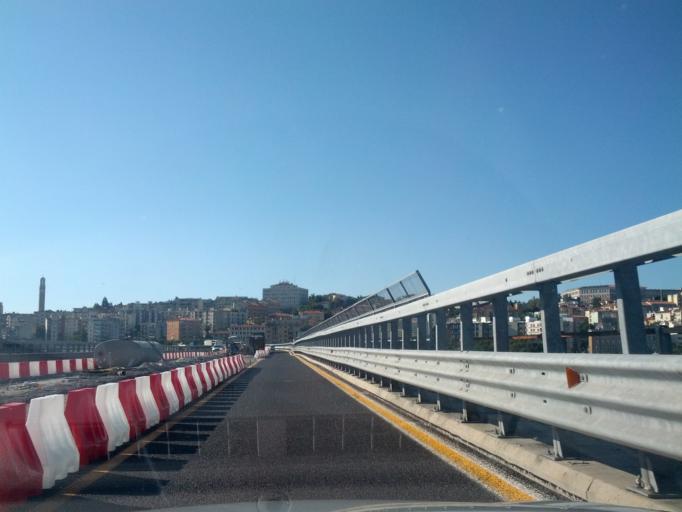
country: IT
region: Friuli Venezia Giulia
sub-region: Provincia di Trieste
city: Trieste
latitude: 45.6366
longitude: 13.7777
